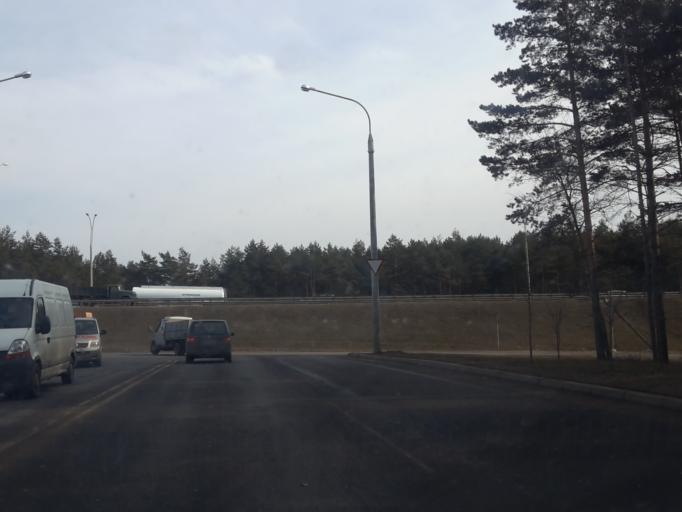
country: BY
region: Minsk
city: Vyaliki Trastsyanets
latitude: 53.9027
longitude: 27.6873
